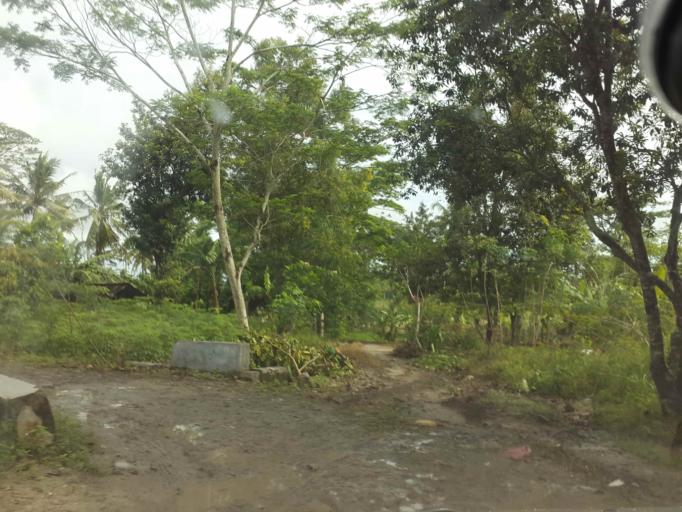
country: ID
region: Lampung
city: Palas
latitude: -5.6327
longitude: 105.6488
